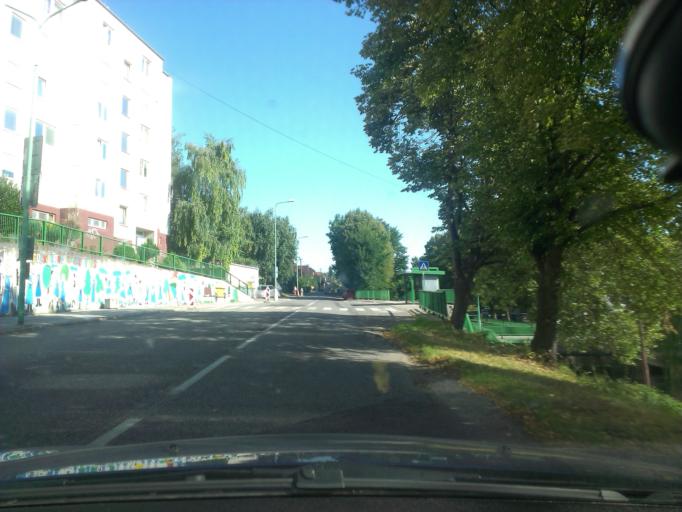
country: SK
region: Trenciansky
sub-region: Okres Myjava
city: Myjava
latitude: 48.7563
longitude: 17.5662
